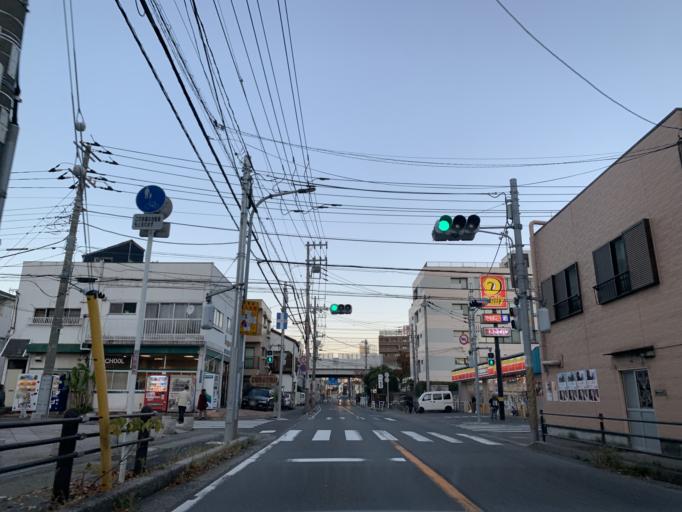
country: JP
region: Chiba
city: Matsudo
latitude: 35.7305
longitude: 139.9013
